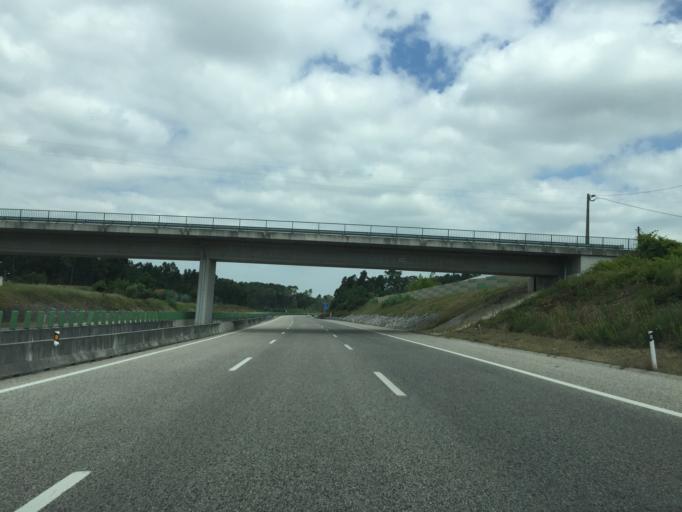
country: PT
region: Leiria
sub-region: Pombal
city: Lourical
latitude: 39.9664
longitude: -8.7781
